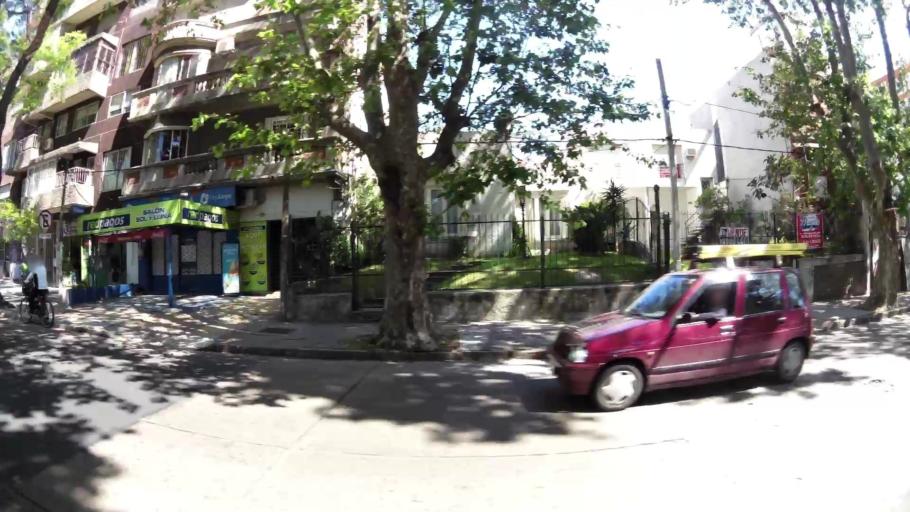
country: UY
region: Montevideo
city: Montevideo
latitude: -34.9028
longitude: -56.1455
